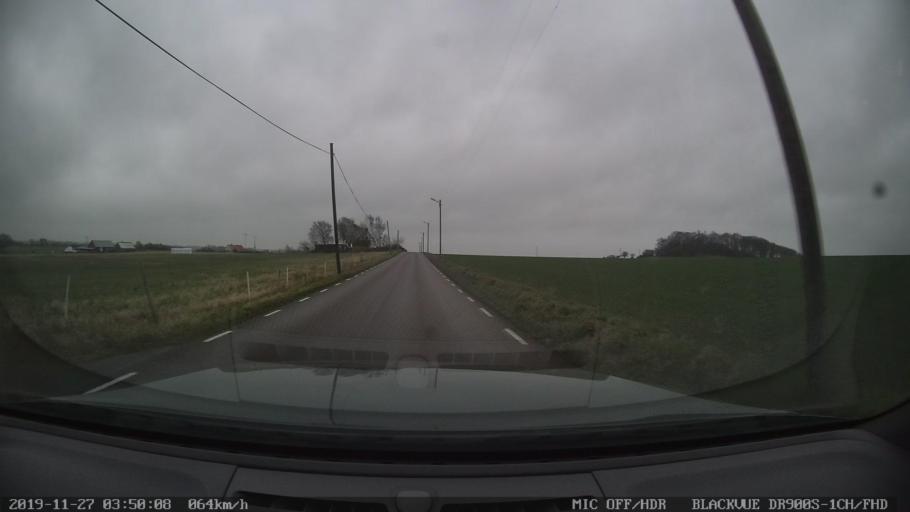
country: SE
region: Skane
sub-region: Hoganas Kommun
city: Hoganas
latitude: 56.2555
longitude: 12.5709
